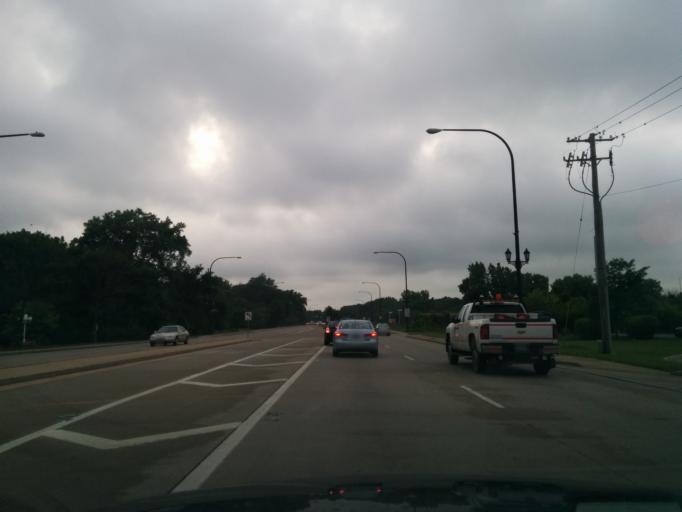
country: US
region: Illinois
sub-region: DuPage County
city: Addison
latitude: 41.9271
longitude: -87.9730
